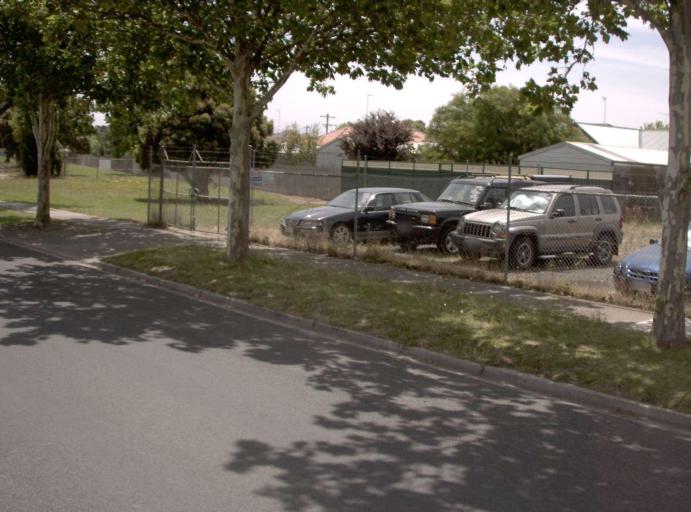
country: AU
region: Victoria
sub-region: Latrobe
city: Moe
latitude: -38.1665
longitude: 146.2629
